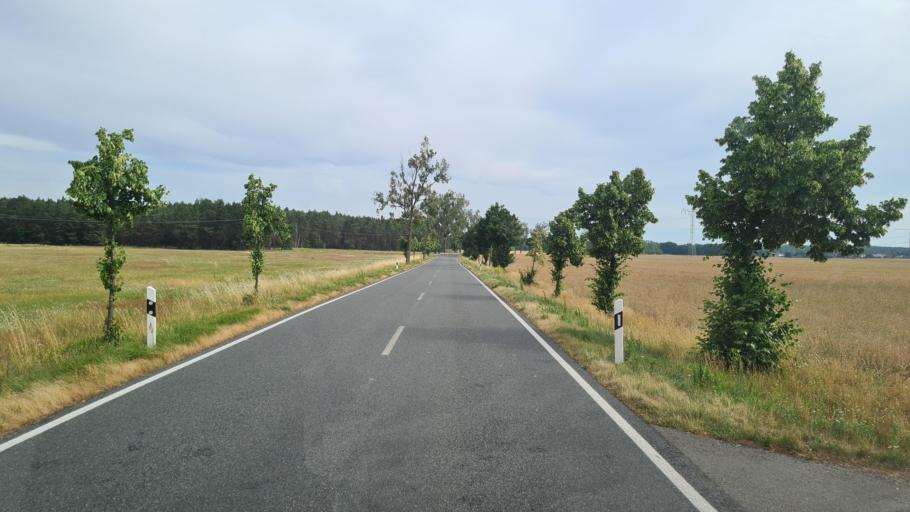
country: DE
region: Saxony-Anhalt
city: Abtsdorf
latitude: 51.8778
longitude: 12.7486
